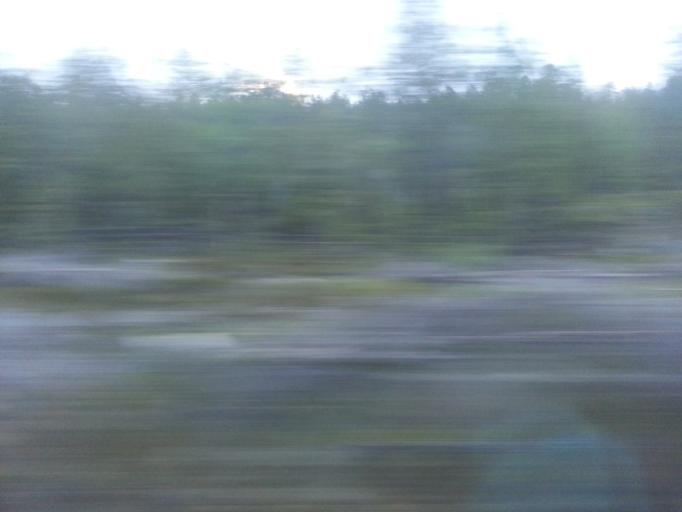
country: NO
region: Oppland
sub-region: Dovre
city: Dombas
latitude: 62.0911
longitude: 9.1411
